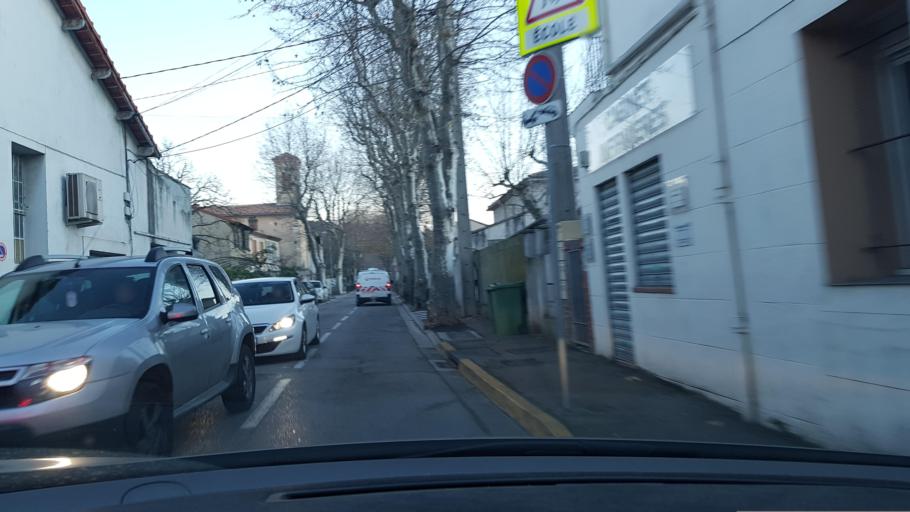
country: FR
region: Provence-Alpes-Cote d'Azur
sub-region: Departement des Bouches-du-Rhone
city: Bouc-Bel-Air
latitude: 43.4845
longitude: 5.4190
